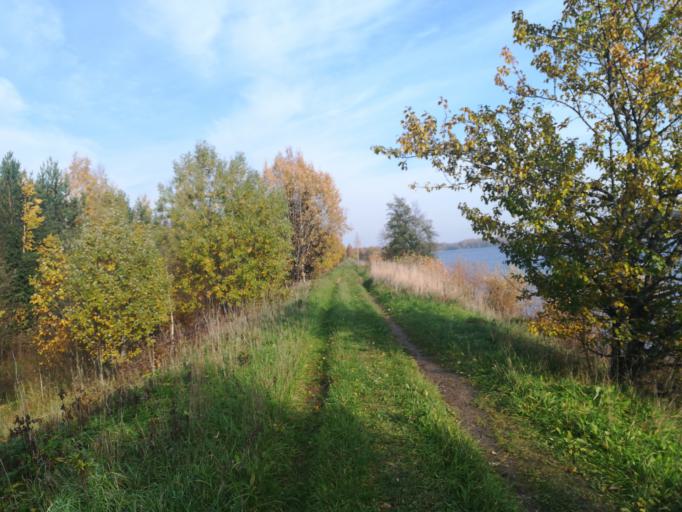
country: RU
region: Leningrad
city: Sista-Palkino
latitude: 59.5899
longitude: 28.8249
